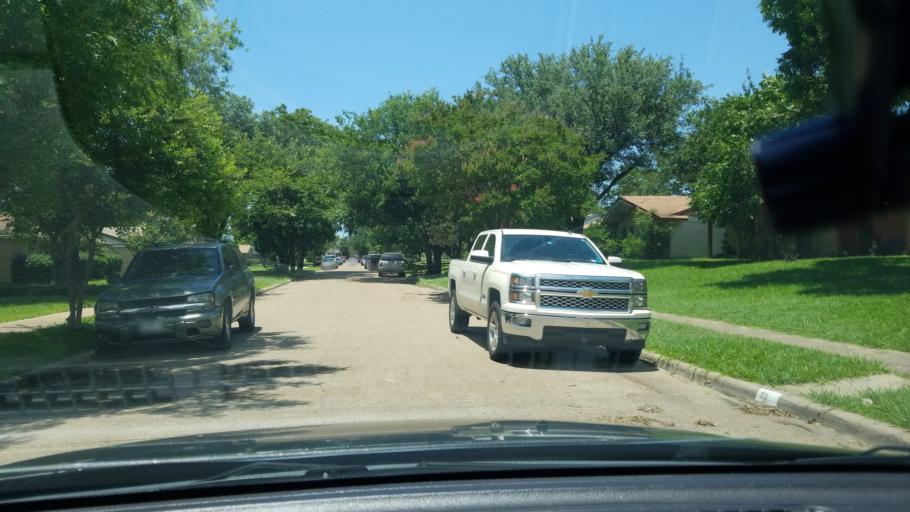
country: US
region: Texas
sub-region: Dallas County
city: Mesquite
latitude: 32.7944
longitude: -96.6490
